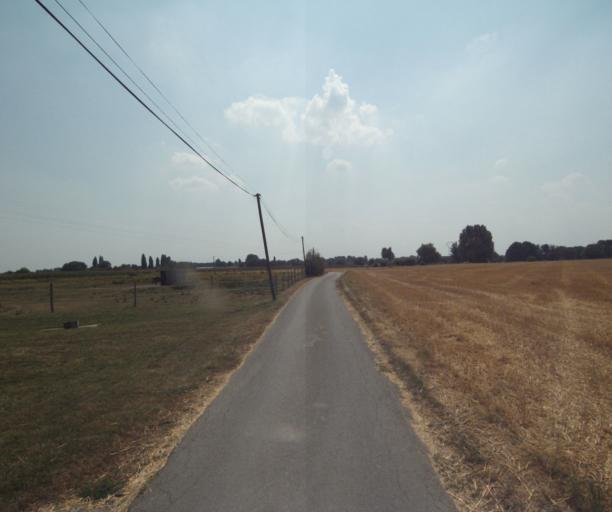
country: FR
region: Nord-Pas-de-Calais
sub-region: Departement du Nord
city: Wambrechies
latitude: 50.7069
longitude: 3.0530
